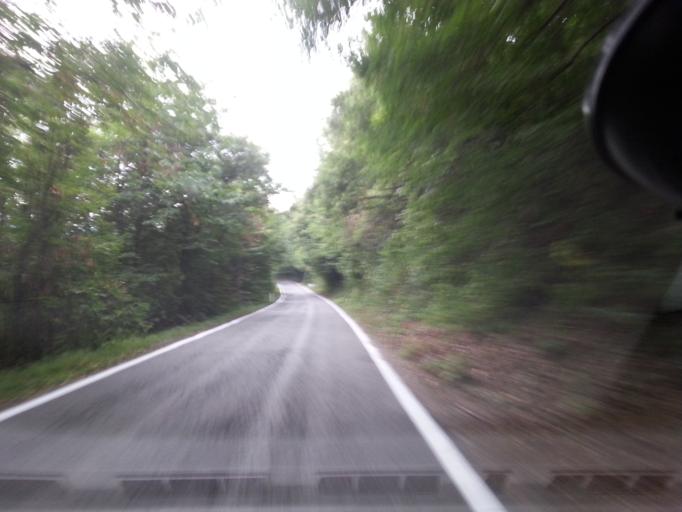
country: IT
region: Piedmont
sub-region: Provincia di Torino
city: Valgioie
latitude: 45.0709
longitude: 7.3623
